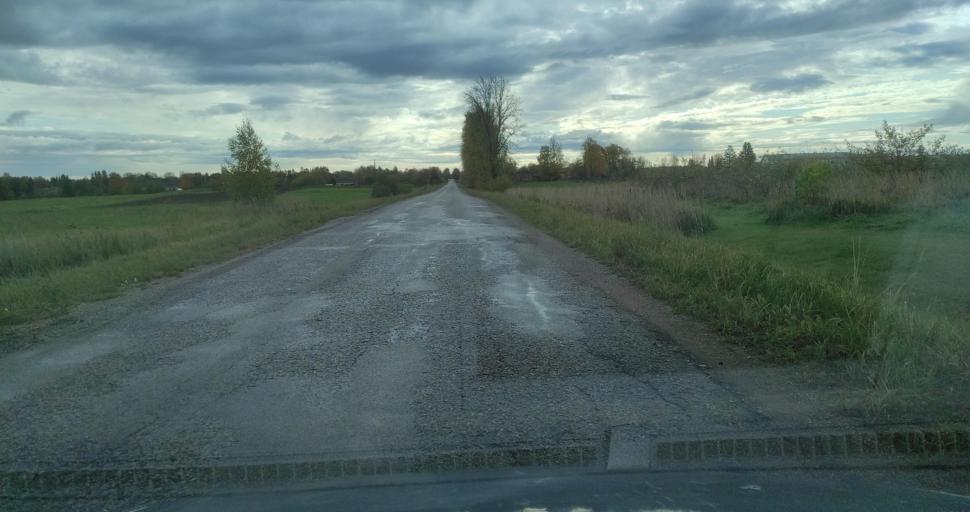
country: LV
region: Vainode
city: Vainode
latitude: 56.5754
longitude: 21.8894
